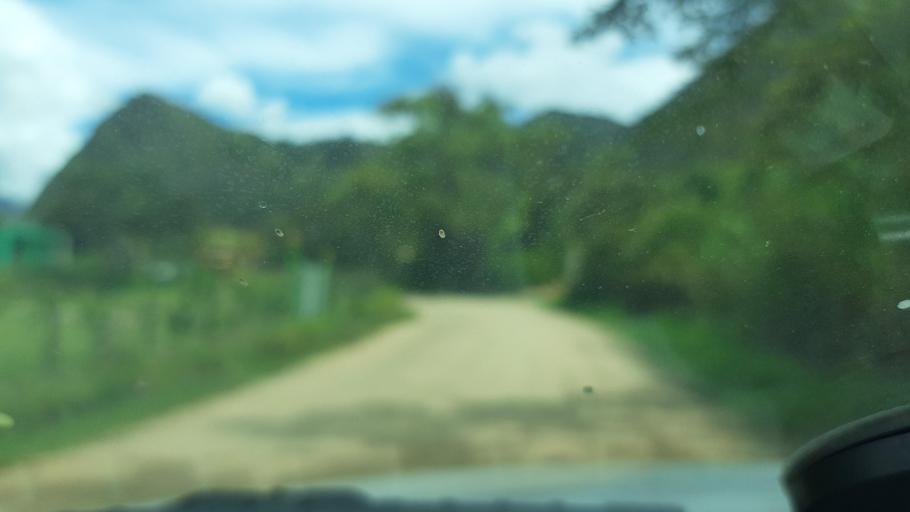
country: CO
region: Cundinamarca
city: Umbita
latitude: 5.2238
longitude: -73.4144
